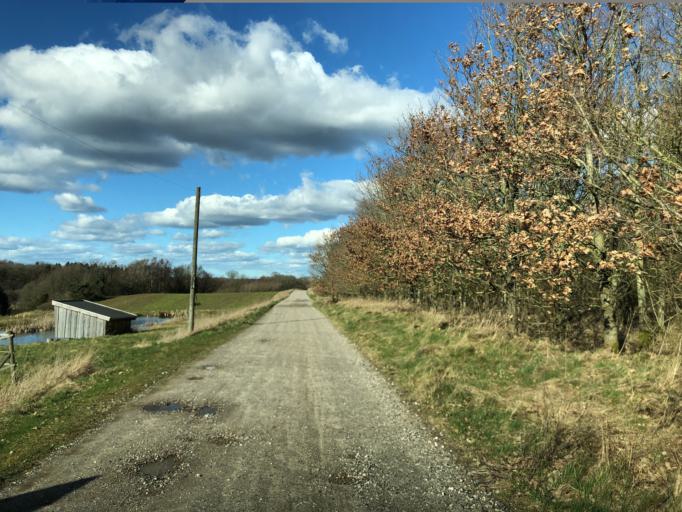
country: DK
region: Central Jutland
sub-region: Favrskov Kommune
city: Hammel
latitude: 56.3159
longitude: 9.9059
